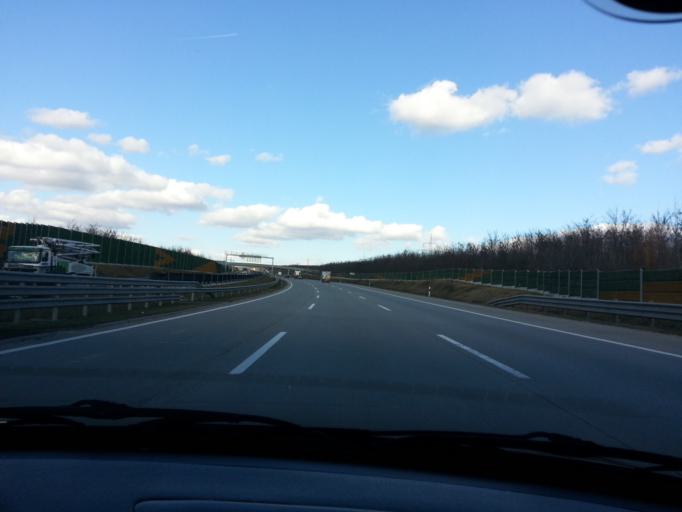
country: HU
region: Pest
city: Ecser
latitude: 47.4416
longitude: 19.3326
